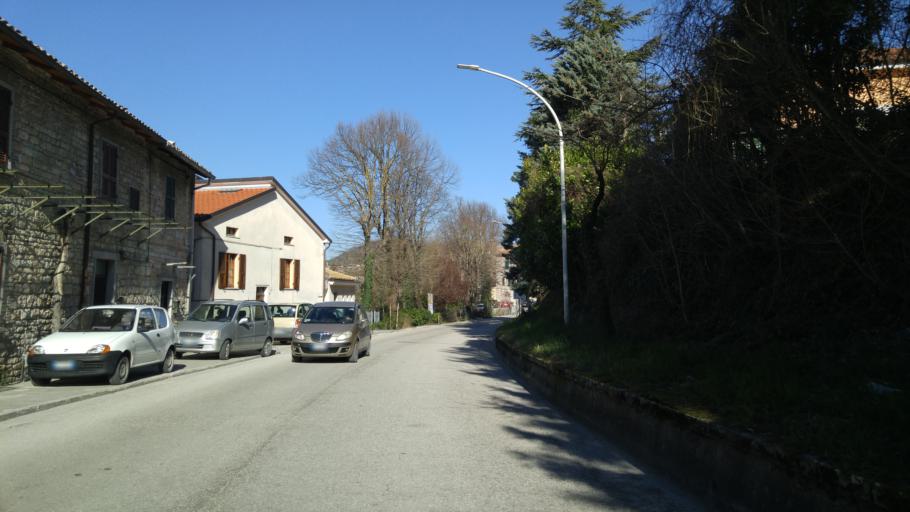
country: IT
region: The Marches
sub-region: Provincia di Pesaro e Urbino
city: Cagli
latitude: 43.5458
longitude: 12.6450
